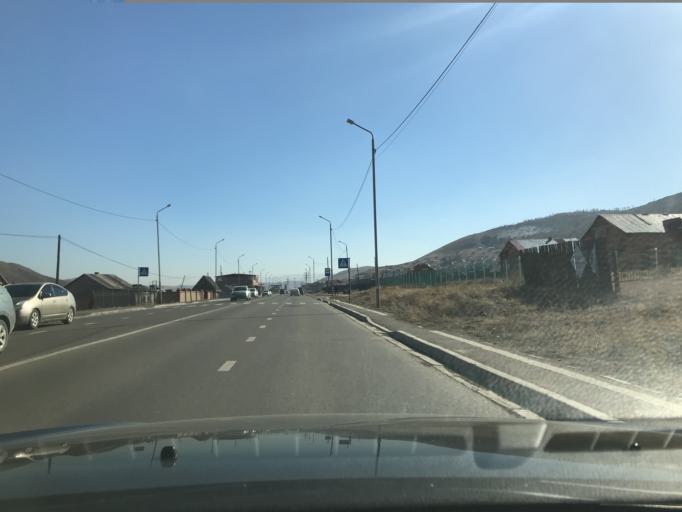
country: MN
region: Ulaanbaatar
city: Ulaanbaatar
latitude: 48.0397
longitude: 106.9049
